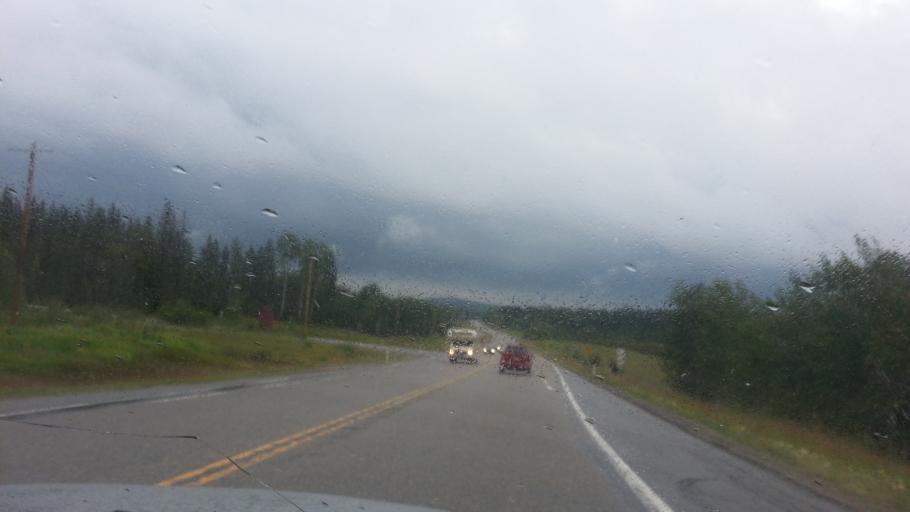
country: CA
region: Alberta
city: Cochrane
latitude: 50.9214
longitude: -114.5850
